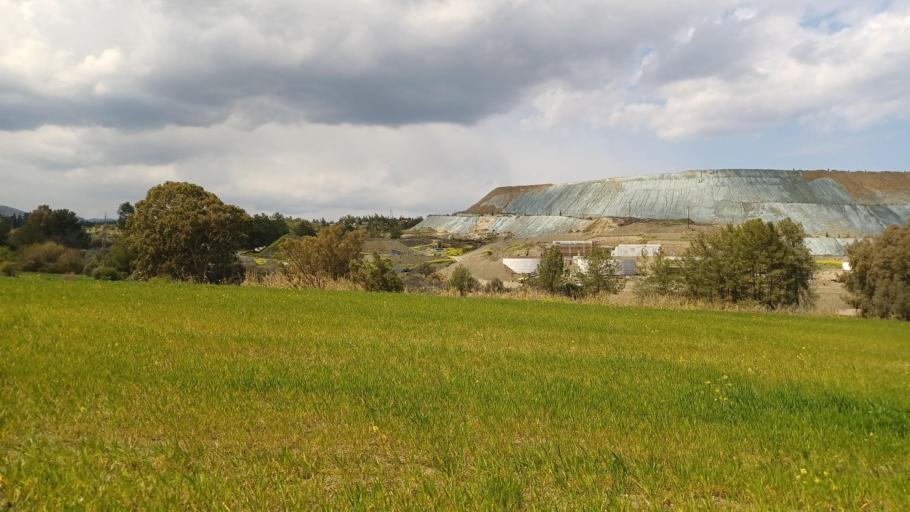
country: CY
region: Lefkosia
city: Lefka
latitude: 35.0845
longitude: 32.9038
